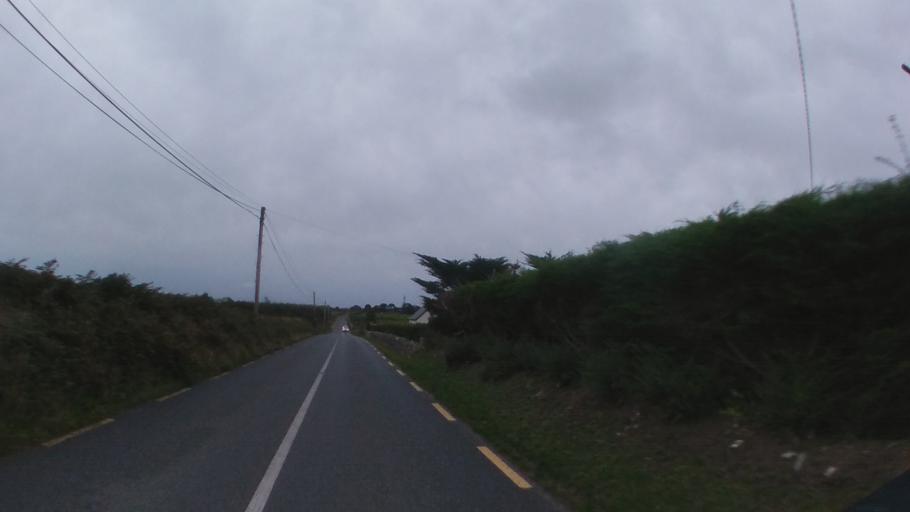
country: IE
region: Leinster
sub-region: Wicklow
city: Kilmacanoge
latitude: 53.1142
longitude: -6.1885
